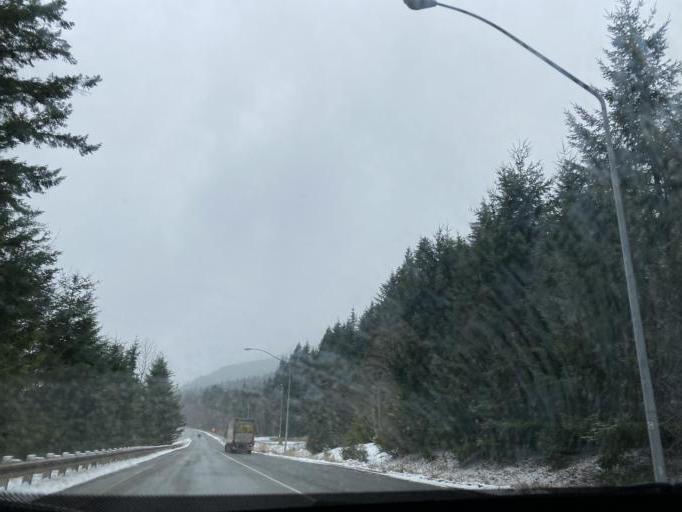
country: US
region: Washington
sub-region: King County
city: Tanner
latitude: 47.3967
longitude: -121.4817
